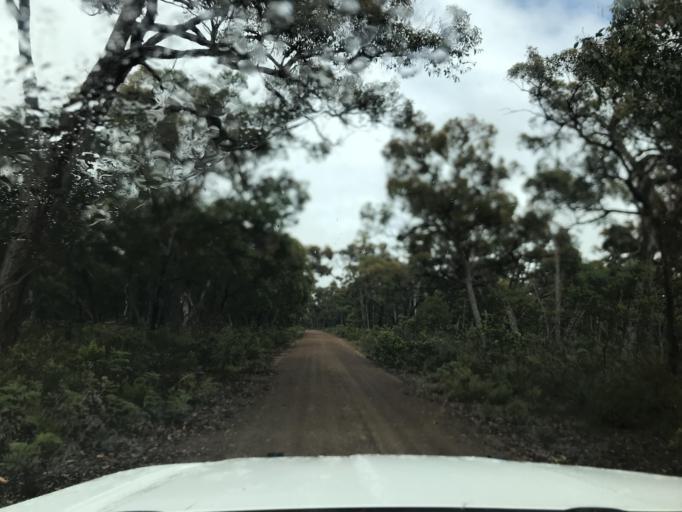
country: AU
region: South Australia
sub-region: Wattle Range
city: Penola
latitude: -37.2592
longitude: 141.3382
